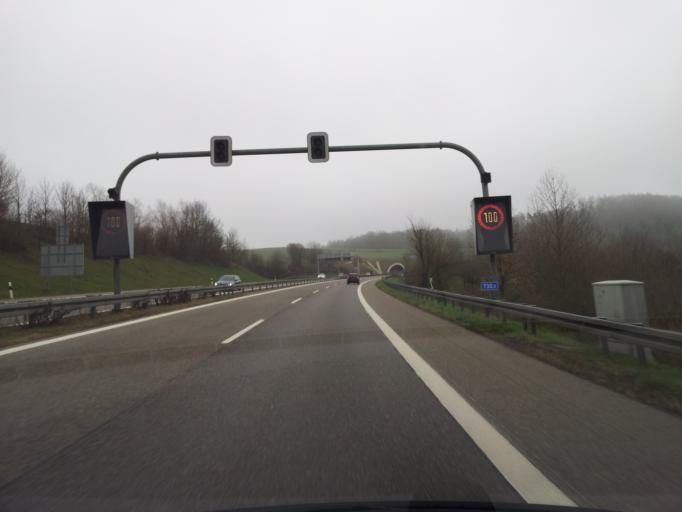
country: DE
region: Baden-Wuerttemberg
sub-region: Freiburg Region
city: Gottmadingen
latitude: 47.7459
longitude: 8.7521
